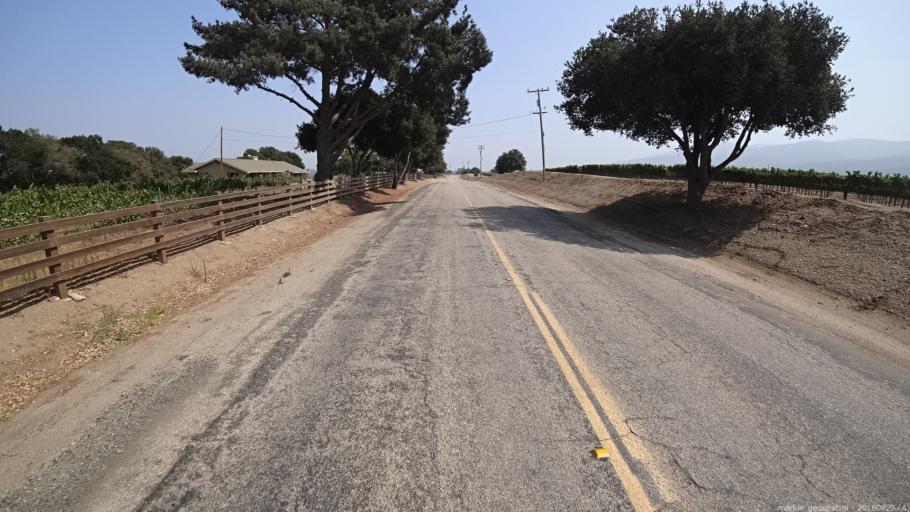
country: US
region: California
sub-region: Monterey County
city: Gonzales
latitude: 36.4548
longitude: -121.4437
